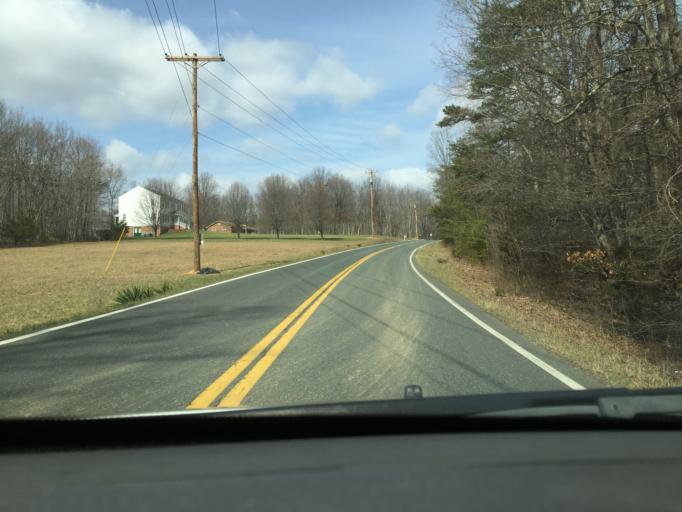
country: US
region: Virginia
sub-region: City of Lynchburg
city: West Lynchburg
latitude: 37.3305
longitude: -79.1664
